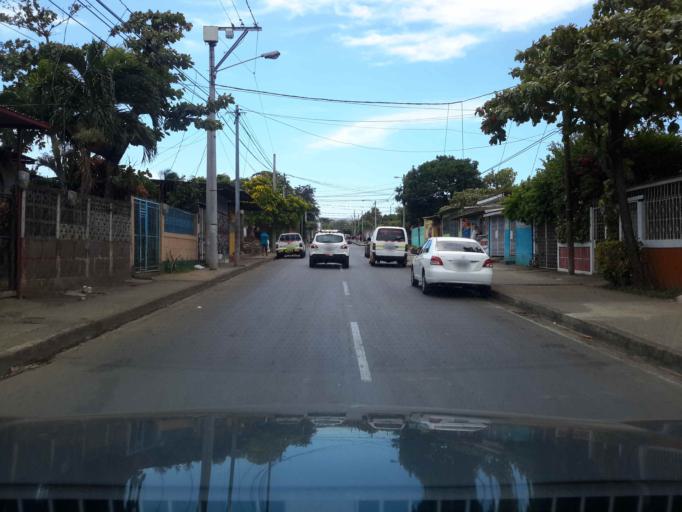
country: NI
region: Managua
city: Managua
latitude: 12.1178
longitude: -86.2974
